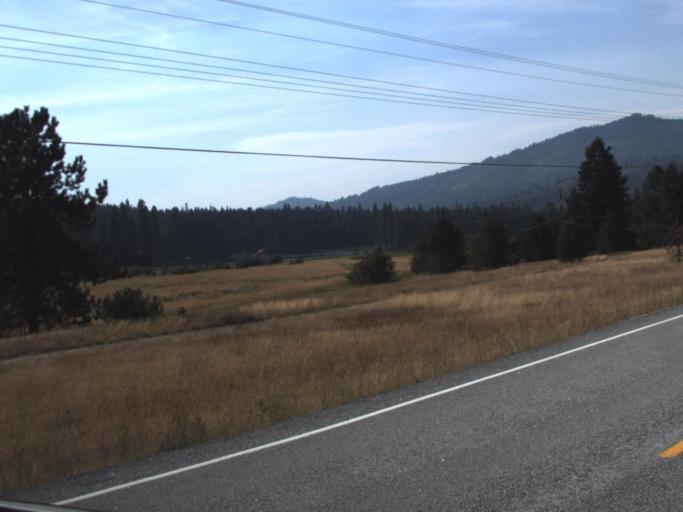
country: US
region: Washington
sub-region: Pend Oreille County
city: Newport
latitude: 48.1486
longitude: -117.2993
